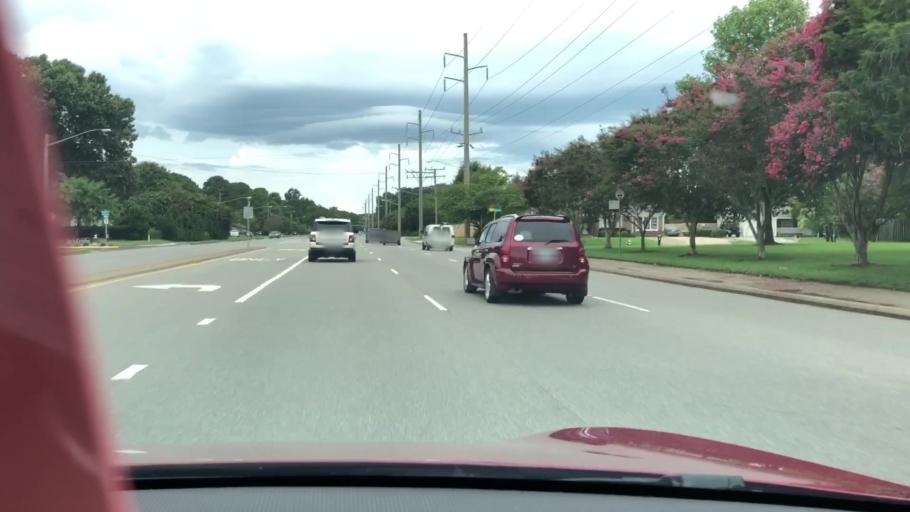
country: US
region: Virginia
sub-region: City of Virginia Beach
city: Virginia Beach
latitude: 36.8809
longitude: -76.0441
